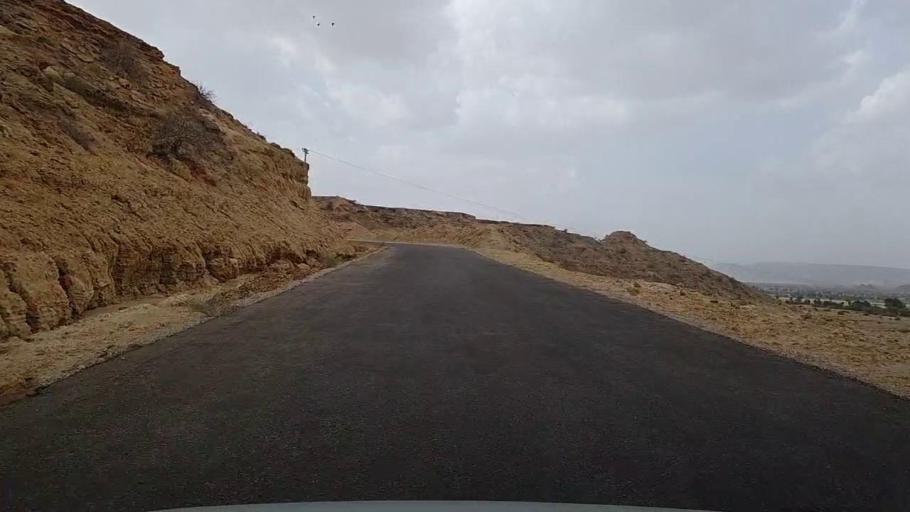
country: PK
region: Sindh
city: Jamshoro
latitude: 25.4268
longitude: 67.6921
